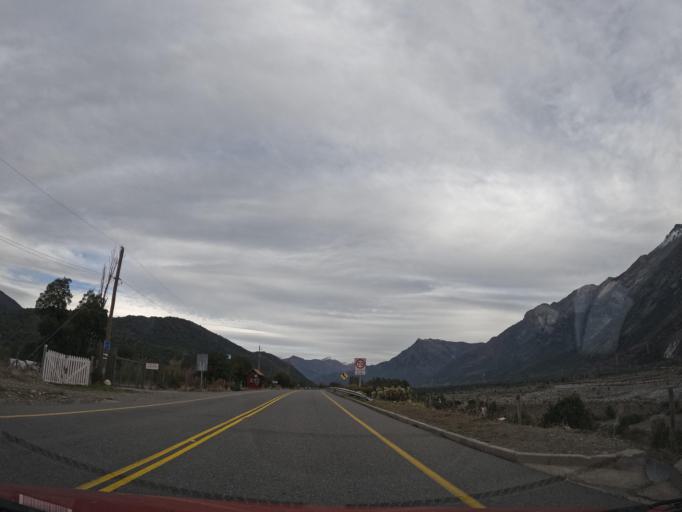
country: CL
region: Maule
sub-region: Provincia de Linares
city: Colbun
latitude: -35.7630
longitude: -71.0033
